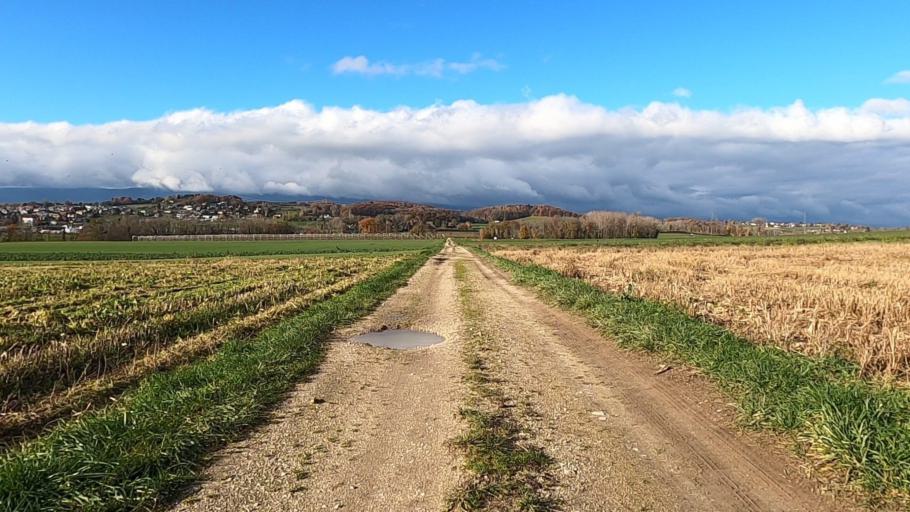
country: CH
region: Vaud
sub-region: Morges District
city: Apples
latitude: 46.5157
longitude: 6.4431
